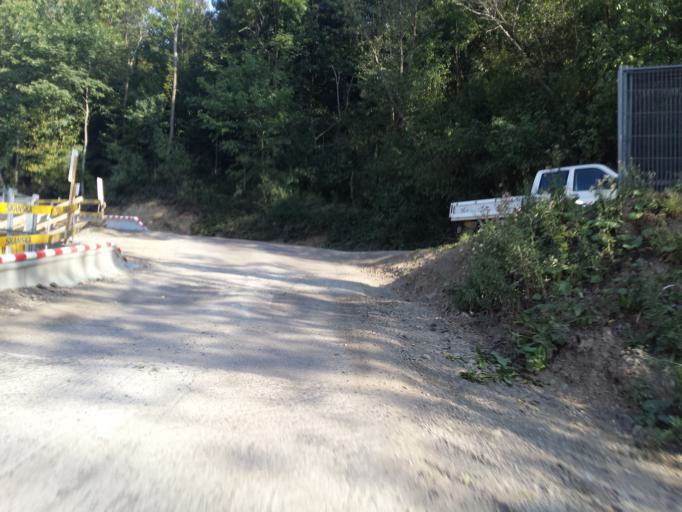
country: PL
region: Subcarpathian Voivodeship
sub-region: Powiat leski
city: Cisna
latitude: 49.2155
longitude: 22.3254
